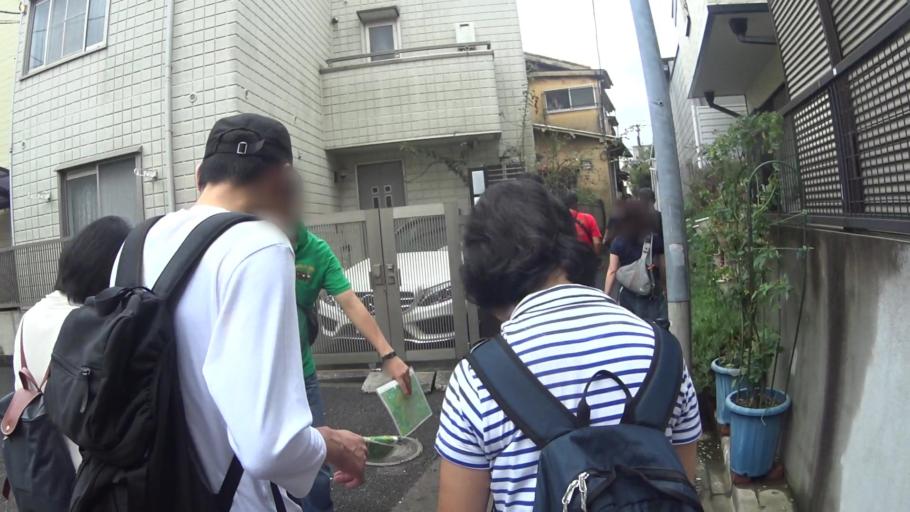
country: JP
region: Tokyo
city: Tokyo
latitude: 35.7325
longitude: 139.6789
